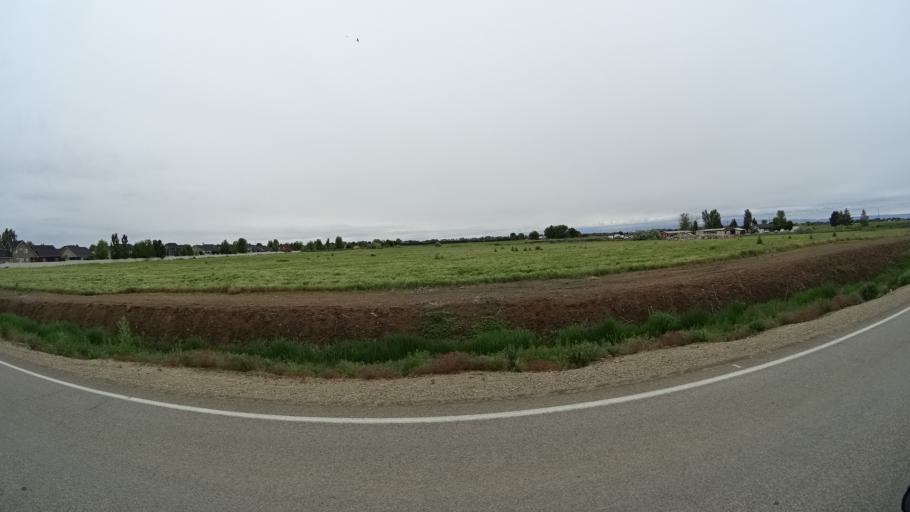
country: US
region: Idaho
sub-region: Ada County
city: Star
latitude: 43.6344
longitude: -116.4622
